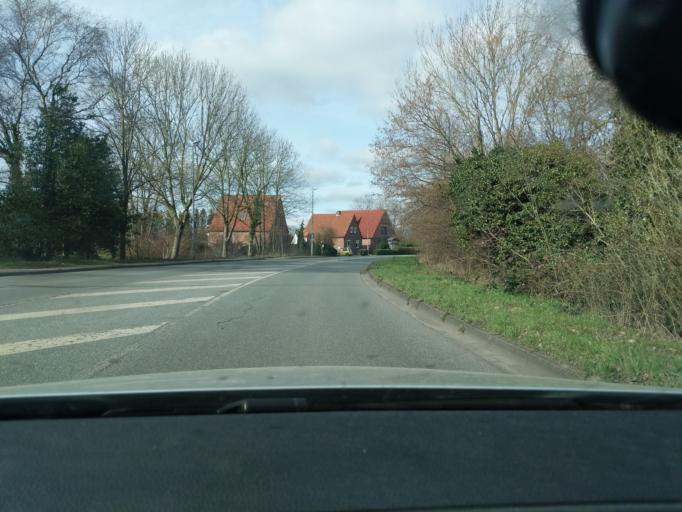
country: DE
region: Lower Saxony
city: Stade
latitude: 53.6561
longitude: 9.4769
